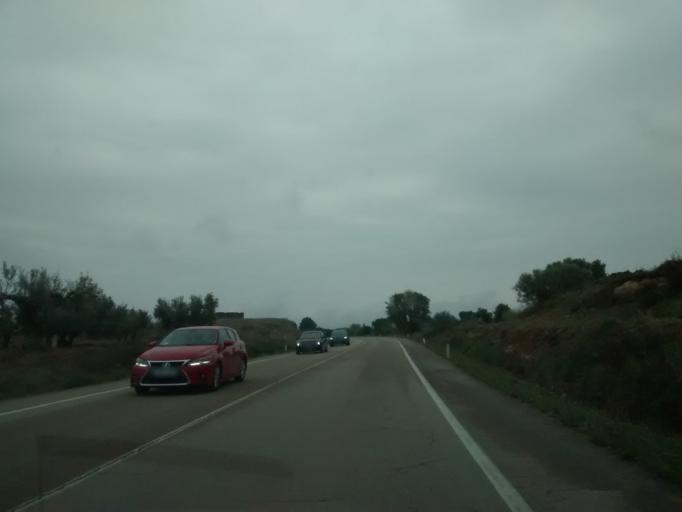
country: ES
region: Aragon
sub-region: Provincia de Zaragoza
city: Caspe
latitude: 41.2216
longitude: -0.0203
